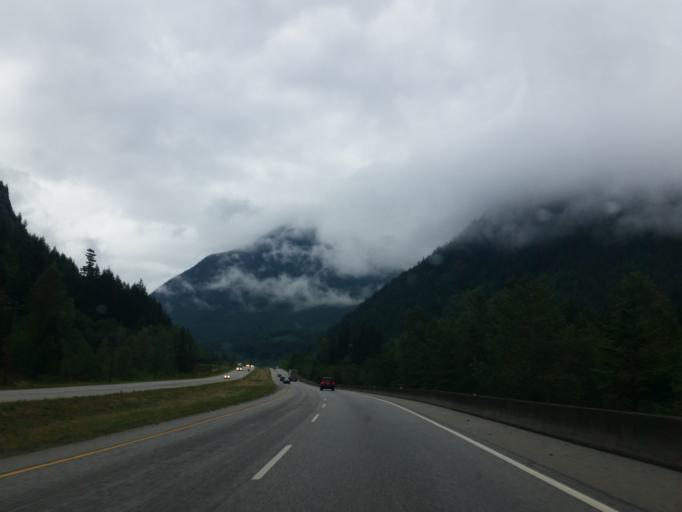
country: CA
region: British Columbia
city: Hope
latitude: 49.4422
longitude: -121.2799
